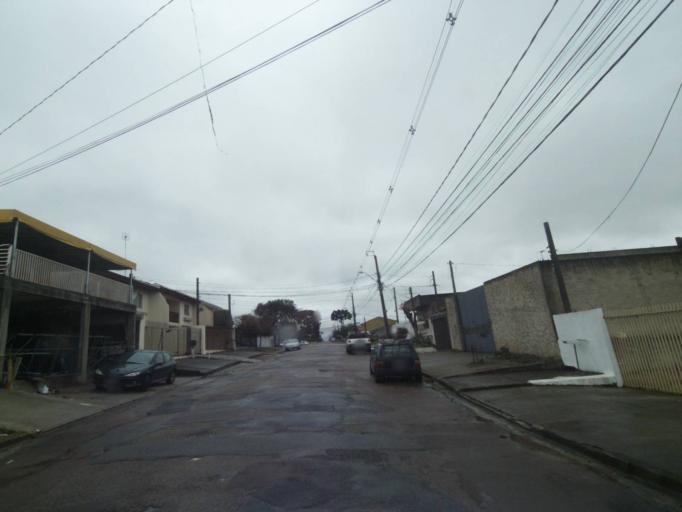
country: BR
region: Parana
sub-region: Curitiba
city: Curitiba
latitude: -25.5161
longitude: -49.3001
